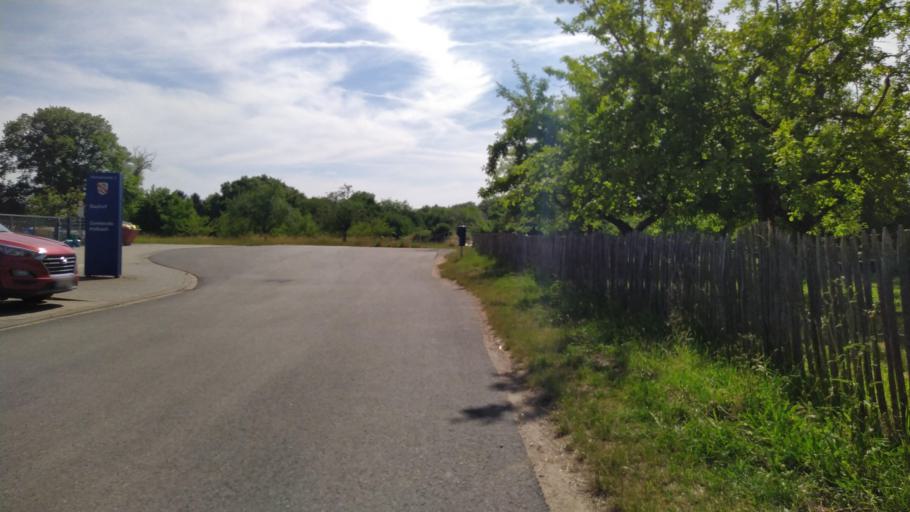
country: DE
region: Bavaria
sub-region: Regierungsbezirk Unterfranken
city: Haibach
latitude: 49.9588
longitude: 9.2038
